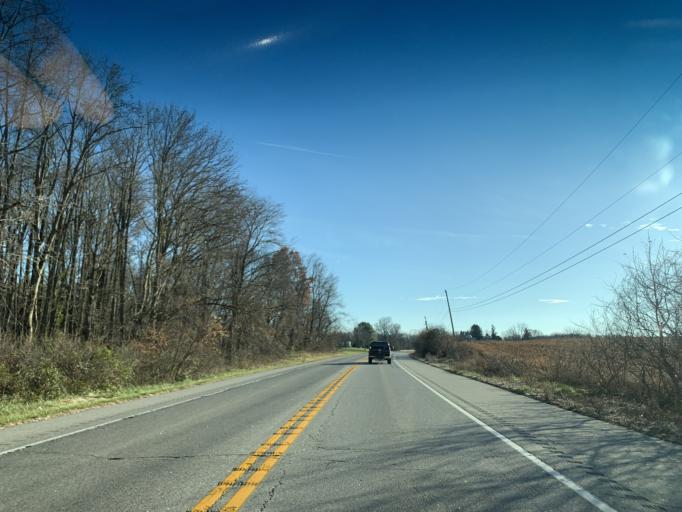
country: US
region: Maryland
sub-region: Cecil County
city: Elkton
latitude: 39.5495
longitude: -75.8027
